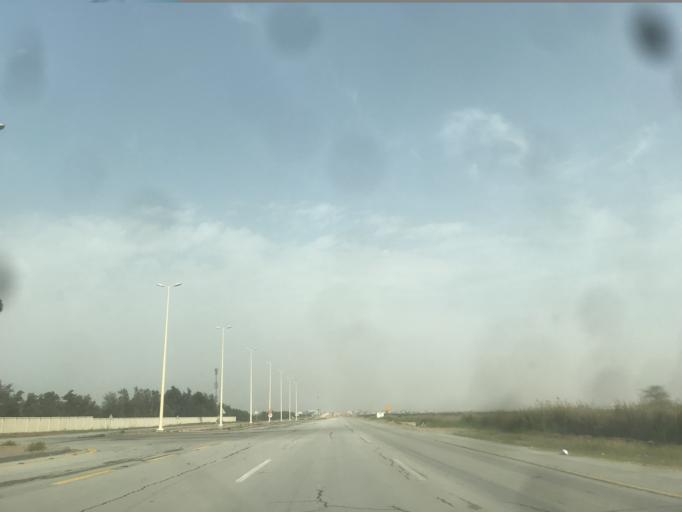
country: SA
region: Eastern Province
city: Dhahran
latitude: 26.1217
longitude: 50.1045
